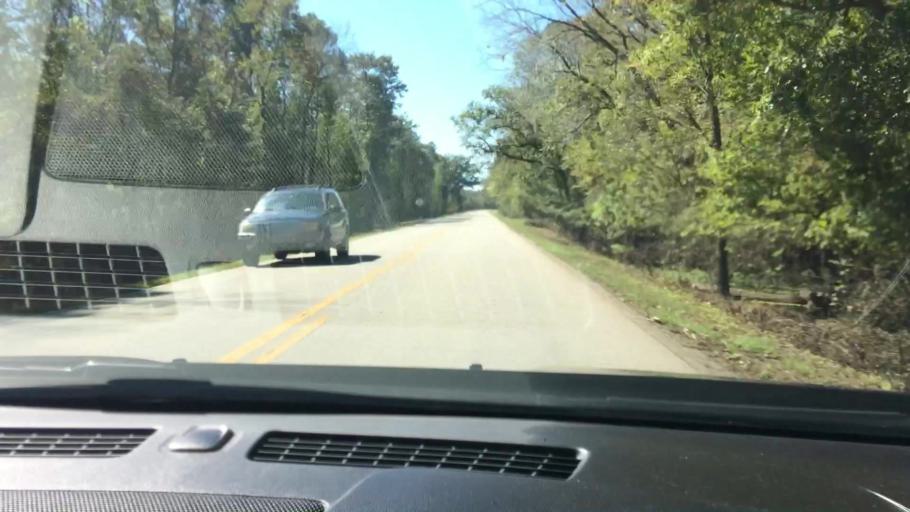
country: US
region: North Carolina
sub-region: Craven County
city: Vanceboro
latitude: 35.3175
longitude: -77.2960
